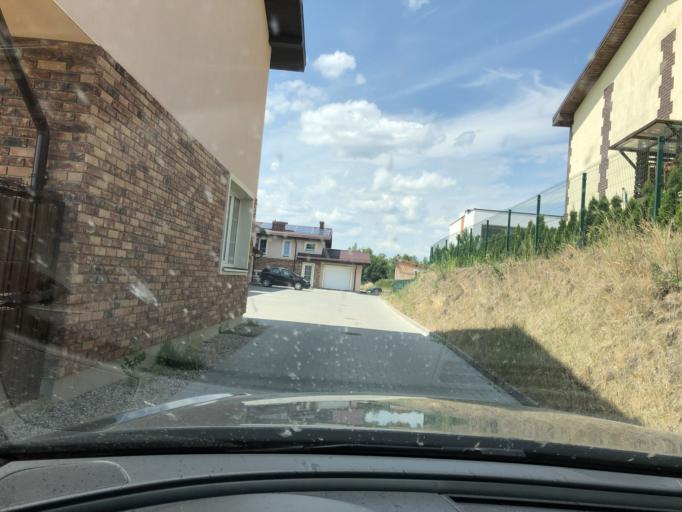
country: LT
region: Vilnius County
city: Pasilaiciai
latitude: 54.7519
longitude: 25.1912
